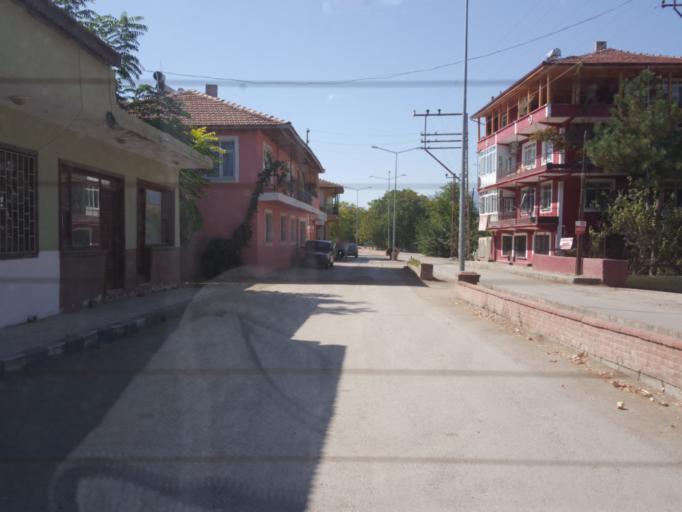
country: TR
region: Amasya
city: Gediksaray
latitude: 40.4460
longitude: 35.6272
